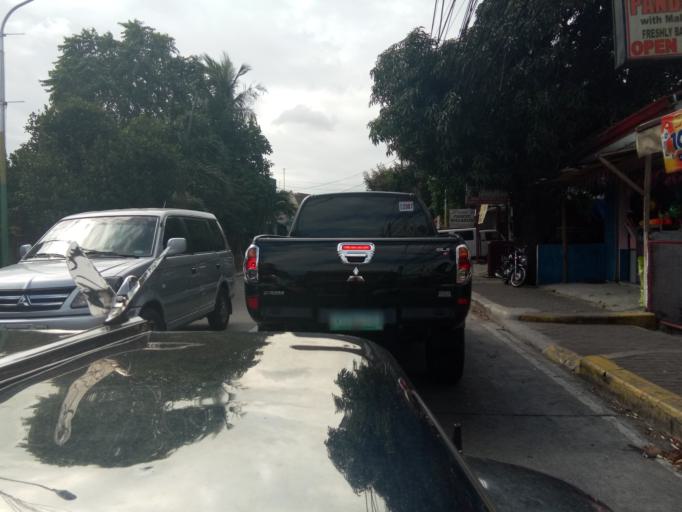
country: PH
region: Calabarzon
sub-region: Province of Cavite
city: Dasmarinas
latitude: 14.3200
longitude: 120.9404
